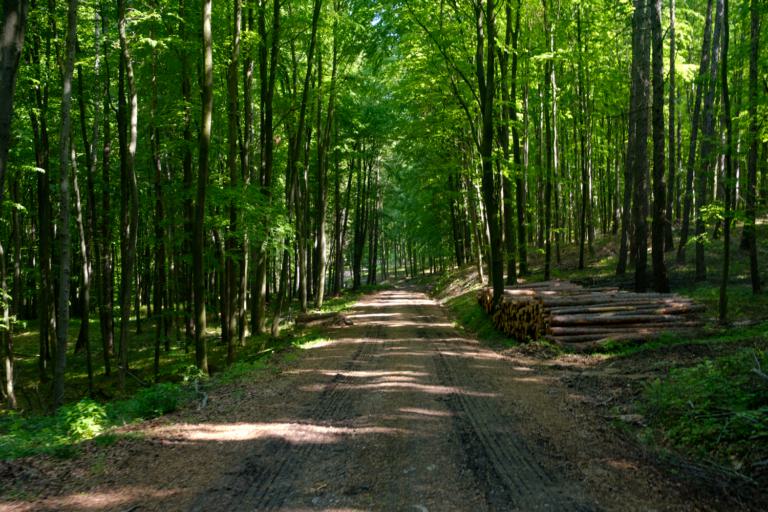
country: HU
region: Veszprem
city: Herend
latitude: 47.2651
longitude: 17.6974
